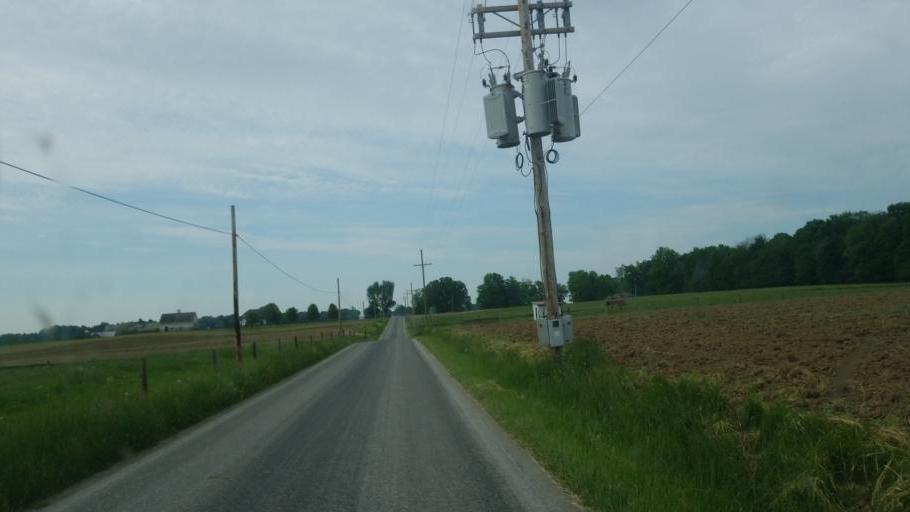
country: US
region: Ohio
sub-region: Wayne County
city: Dalton
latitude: 40.7399
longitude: -81.7549
